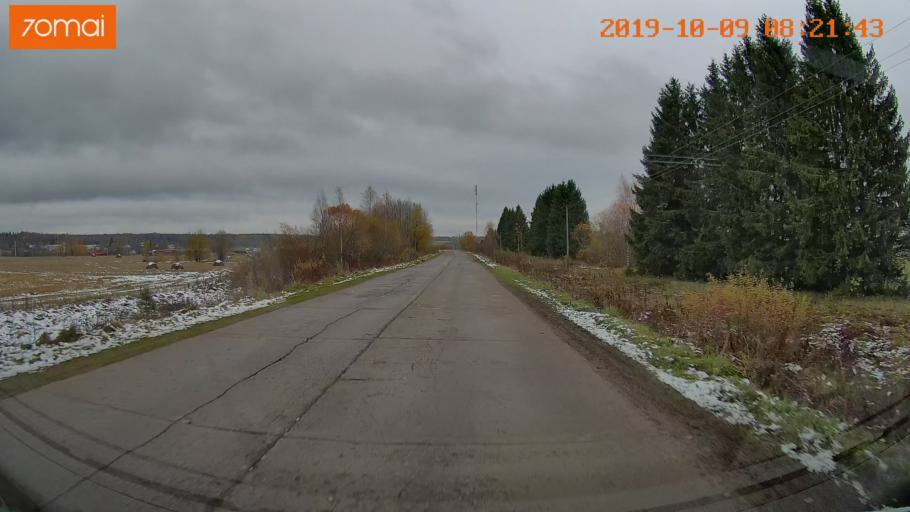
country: RU
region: Vologda
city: Gryazovets
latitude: 58.7419
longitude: 40.2818
